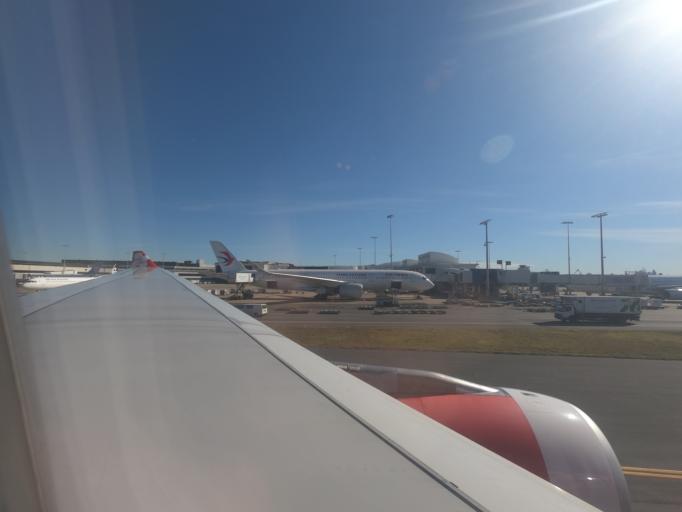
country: AU
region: New South Wales
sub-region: Rockdale
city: Arncliffe
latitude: -33.9404
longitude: 151.1692
